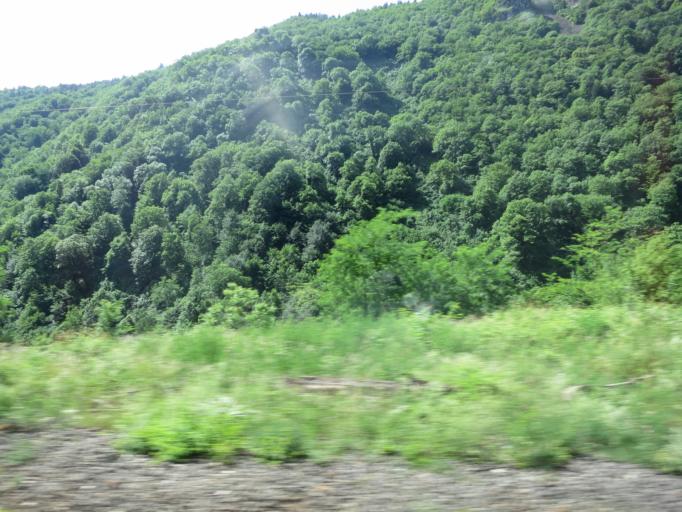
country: GE
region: Samtskhe-Javakheti
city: Borjomi
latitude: 41.9951
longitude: 43.4035
